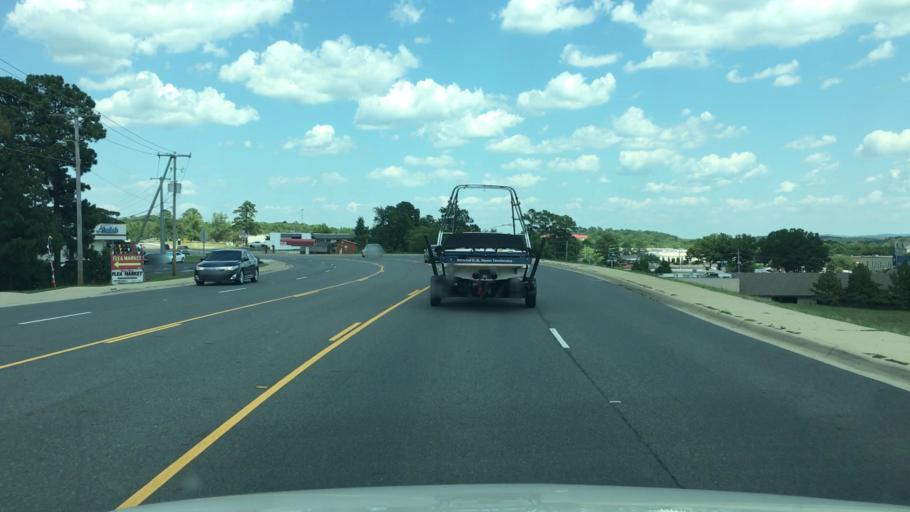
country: US
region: Arkansas
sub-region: Garland County
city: Lake Hamilton
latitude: 34.4502
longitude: -93.0842
